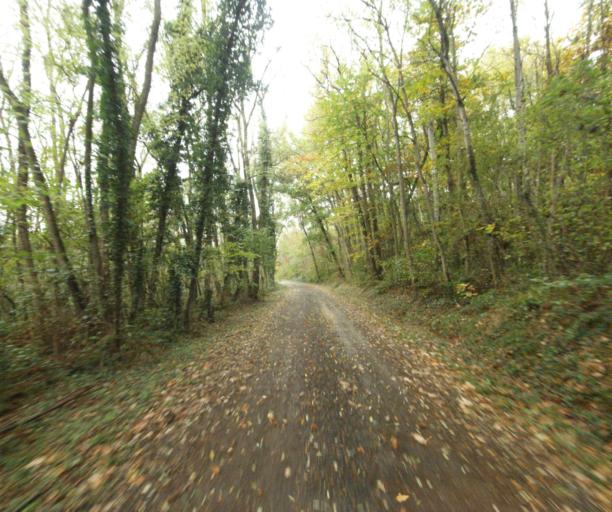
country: FR
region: Bourgogne
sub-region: Departement de Saone-et-Loire
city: Tournus
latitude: 46.4839
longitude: 4.8522
